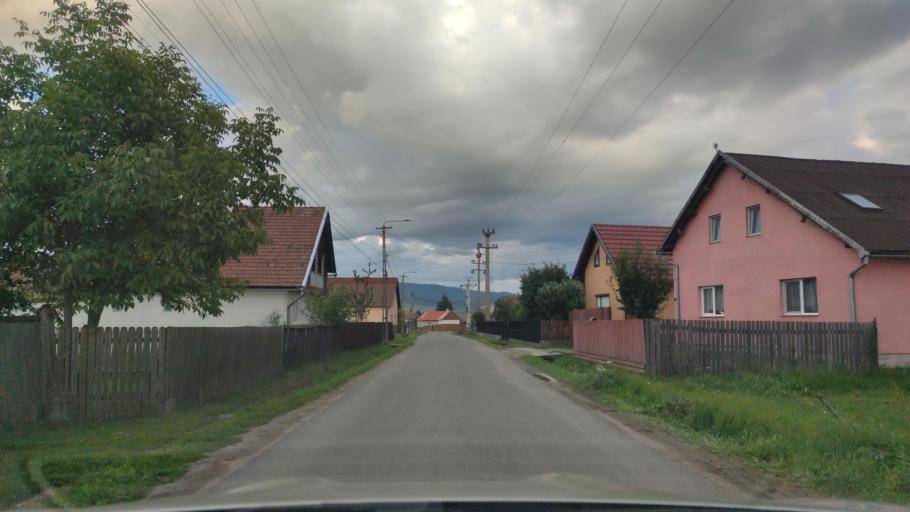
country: RO
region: Harghita
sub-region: Comuna Remetea
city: Remetea
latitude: 46.8047
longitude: 25.4474
